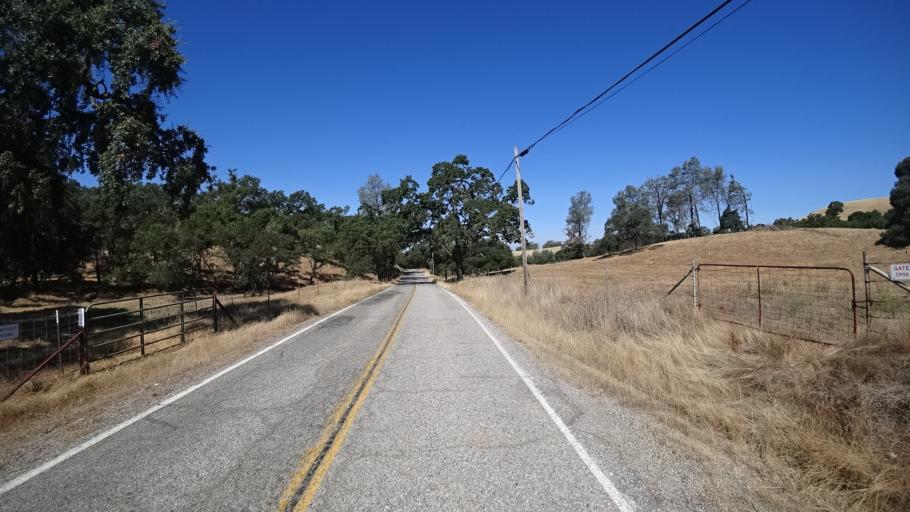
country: US
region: California
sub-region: Calaveras County
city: Valley Springs
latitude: 38.2295
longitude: -120.8467
